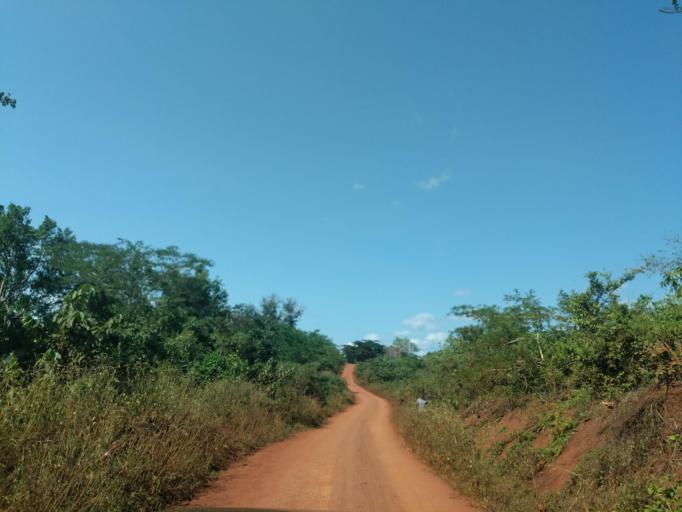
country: TZ
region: Tanga
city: Muheza
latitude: -5.3784
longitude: 38.5811
